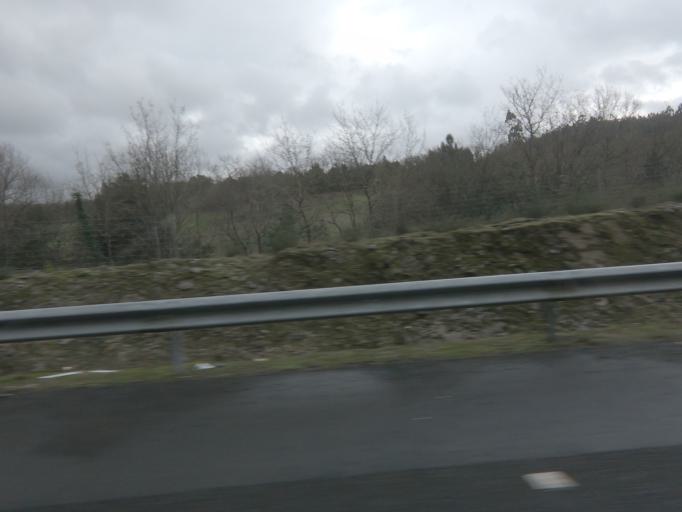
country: ES
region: Galicia
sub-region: Provincia da Coruna
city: Vedra
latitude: 42.7960
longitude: -8.4833
